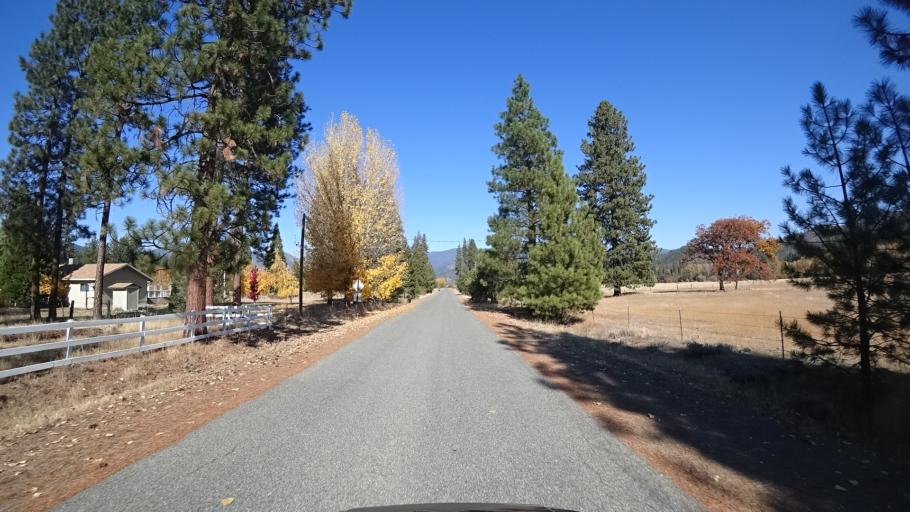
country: US
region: California
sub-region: Siskiyou County
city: Yreka
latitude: 41.6048
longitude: -122.9698
